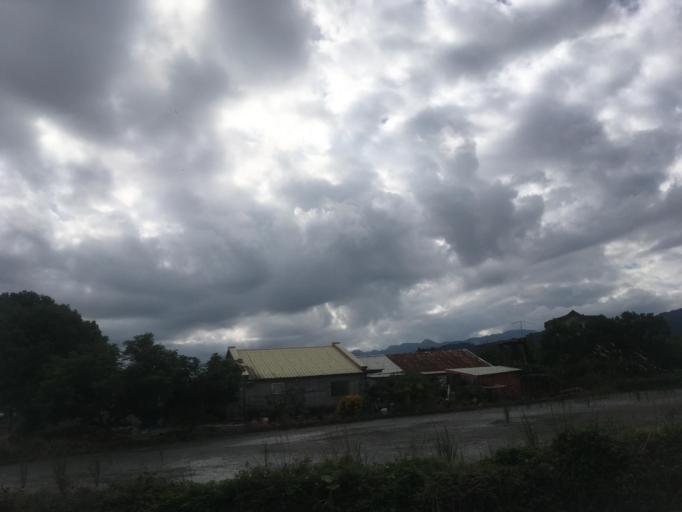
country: TW
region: Taiwan
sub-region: Yilan
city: Yilan
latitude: 24.6826
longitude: 121.6918
